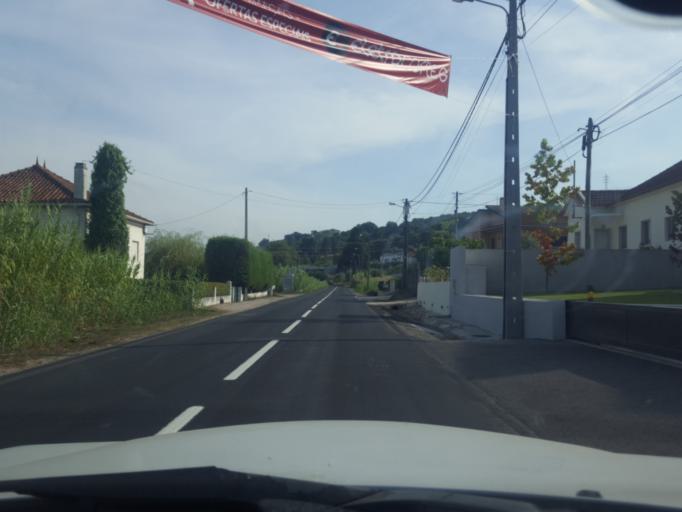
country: PT
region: Leiria
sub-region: Leiria
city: Leiria
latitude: 39.7068
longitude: -8.7929
